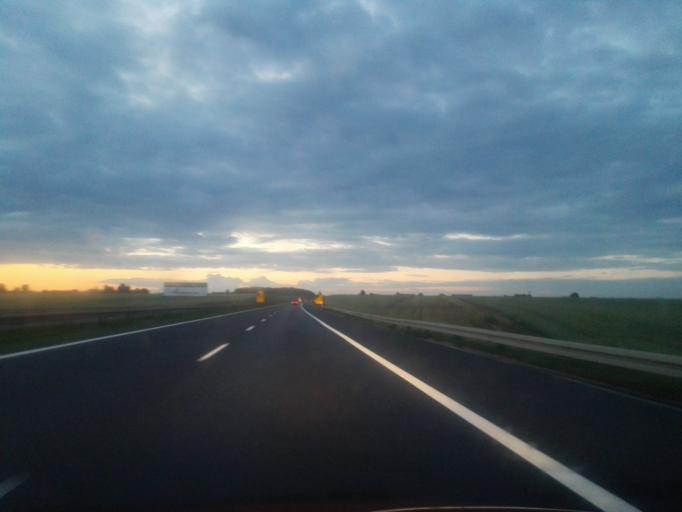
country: PL
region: Lodz Voivodeship
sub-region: Powiat piotrkowski
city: Grabica
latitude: 51.5251
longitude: 19.5996
